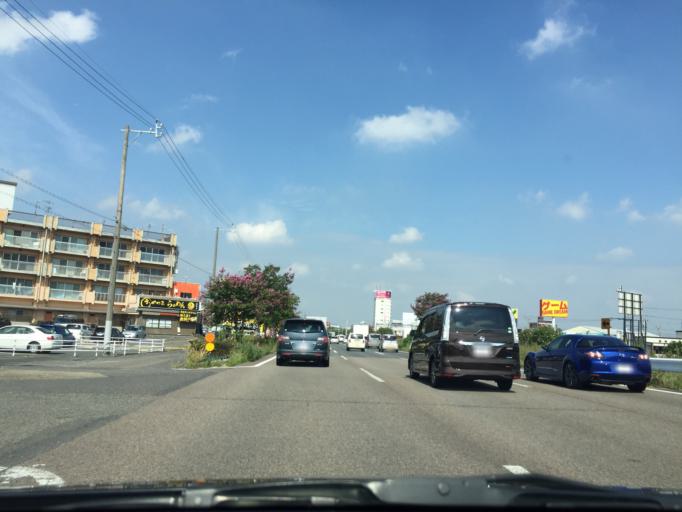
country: JP
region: Gifu
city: Gifu-shi
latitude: 35.3925
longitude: 136.7360
